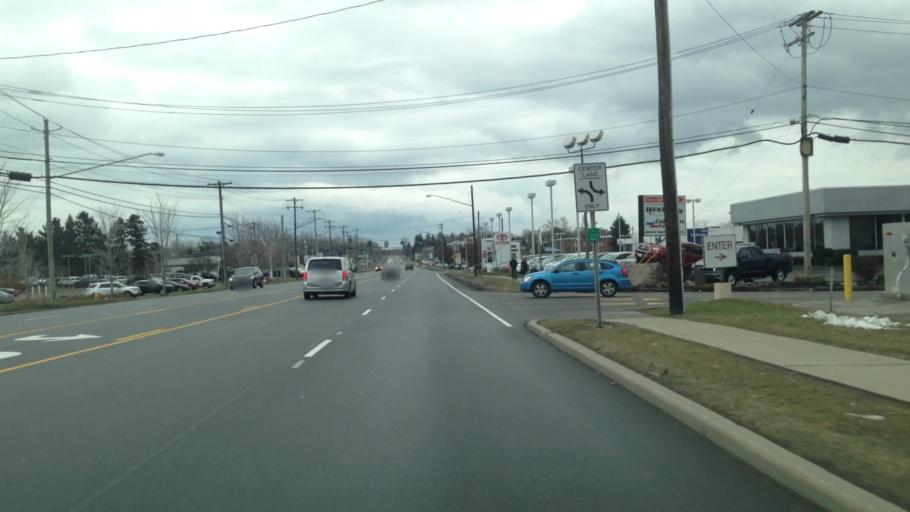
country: US
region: New York
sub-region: Erie County
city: Harris Hill
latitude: 42.9651
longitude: -78.6944
